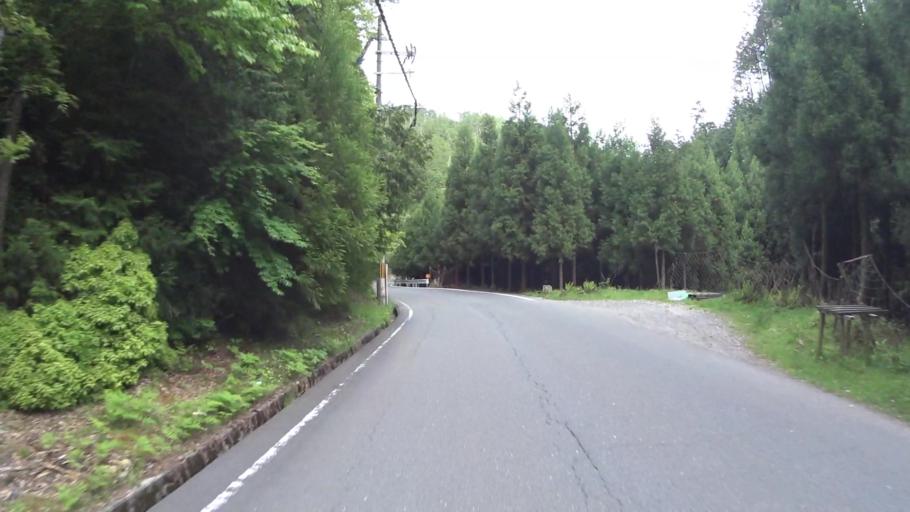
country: JP
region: Kyoto
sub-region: Kyoto-shi
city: Kamigyo-ku
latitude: 35.1874
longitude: 135.6456
